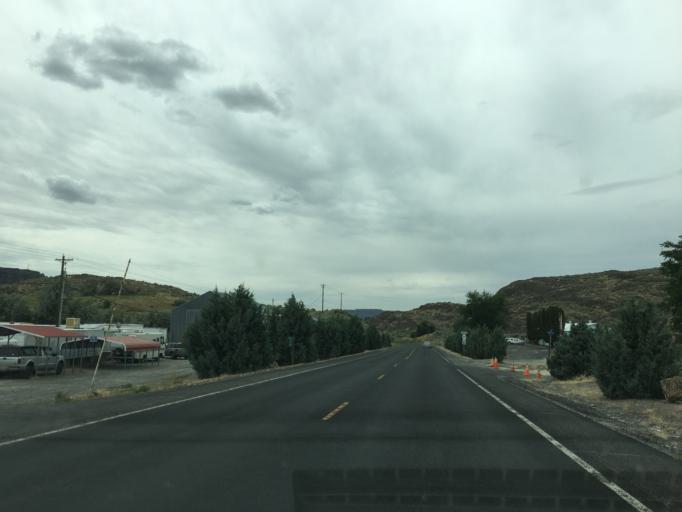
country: US
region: Washington
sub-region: Okanogan County
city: Coulee Dam
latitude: 47.9302
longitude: -119.0422
